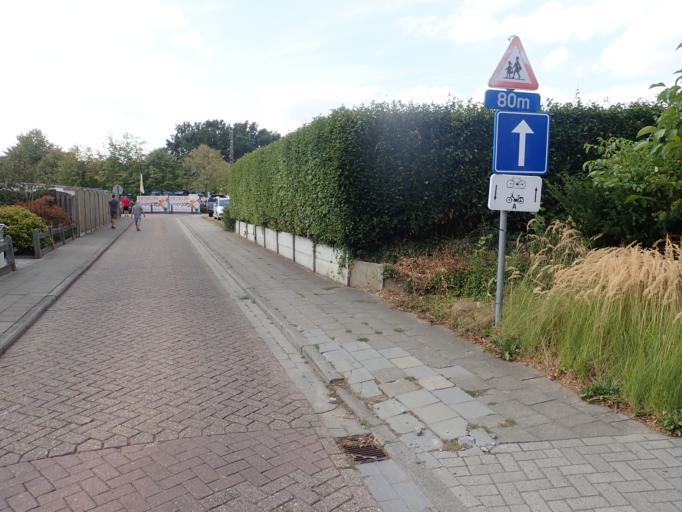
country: BE
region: Flanders
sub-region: Provincie Antwerpen
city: Herselt
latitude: 51.0550
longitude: 4.8827
